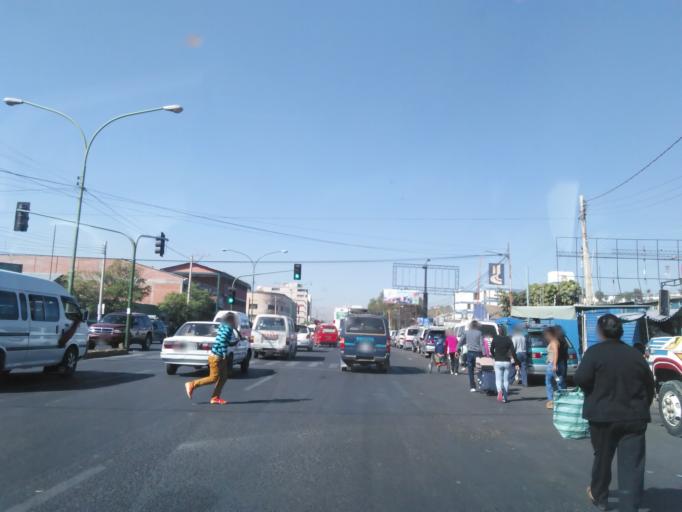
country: BO
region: Cochabamba
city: Cochabamba
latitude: -17.4007
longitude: -66.1577
